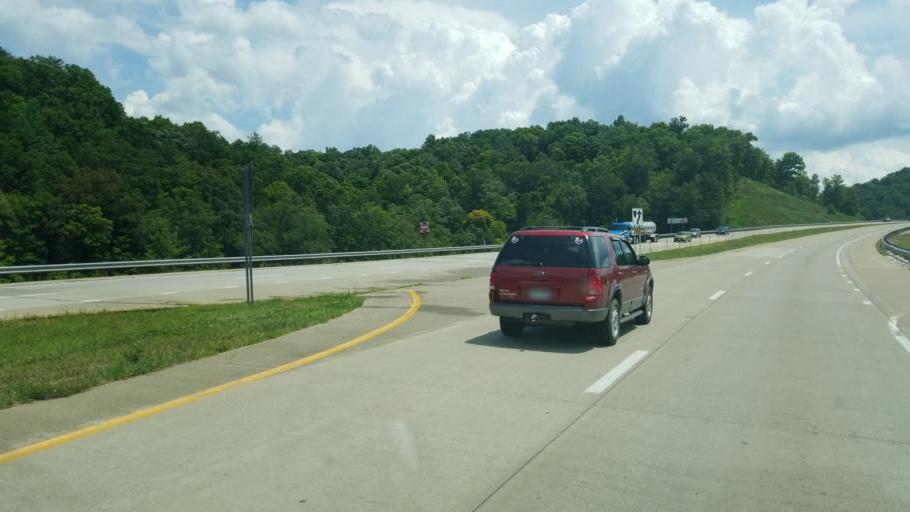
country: US
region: West Virginia
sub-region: Putnam County
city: Eleanor
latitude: 38.5236
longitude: -81.9351
